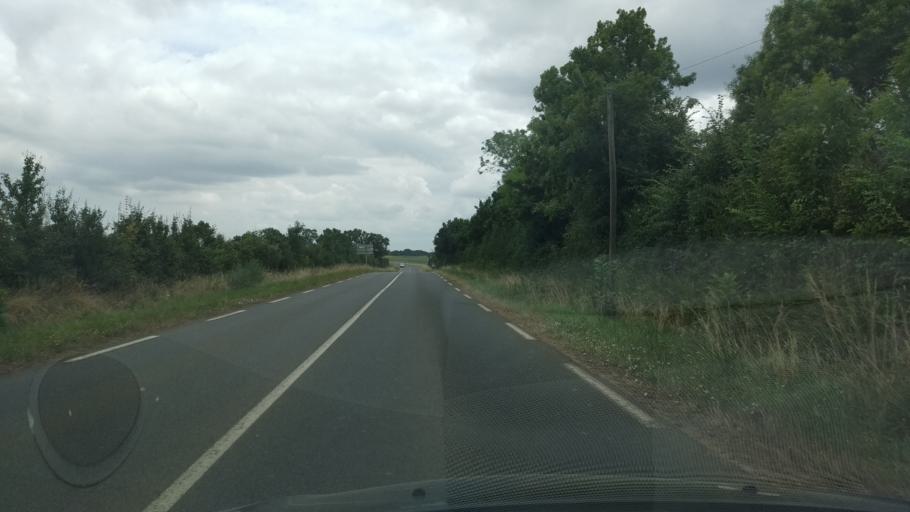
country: FR
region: Poitou-Charentes
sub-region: Departement de la Vienne
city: La Villedieu-du-Clain
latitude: 46.4416
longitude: 0.3706
